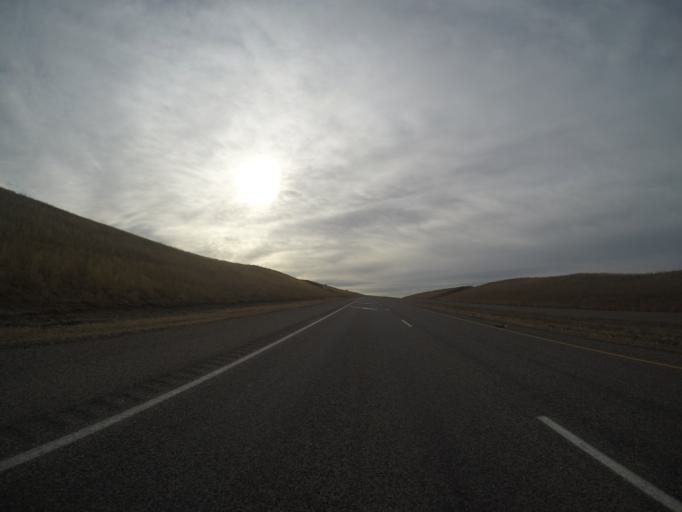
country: US
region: Montana
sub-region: Yellowstone County
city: Laurel
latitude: 45.6040
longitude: -108.8227
